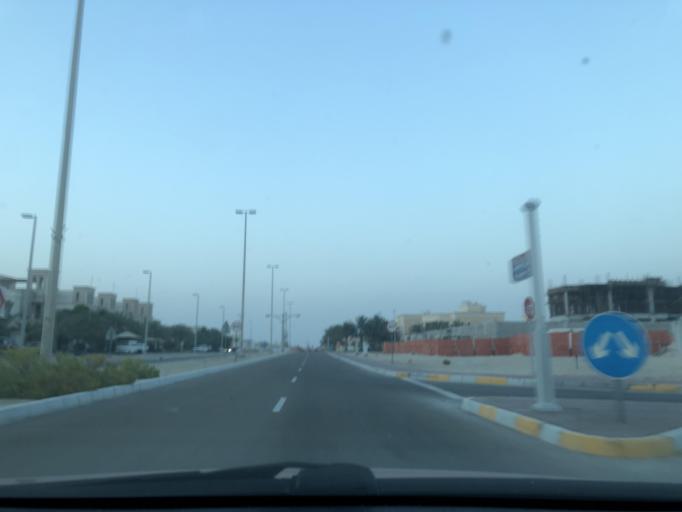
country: AE
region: Abu Dhabi
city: Abu Dhabi
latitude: 24.3515
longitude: 54.6238
